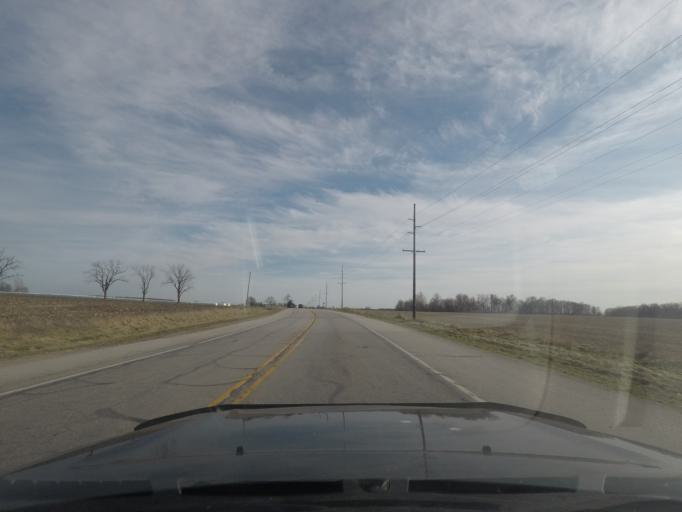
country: US
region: Indiana
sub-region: Elkhart County
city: Wakarusa
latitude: 41.5050
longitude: -86.0014
